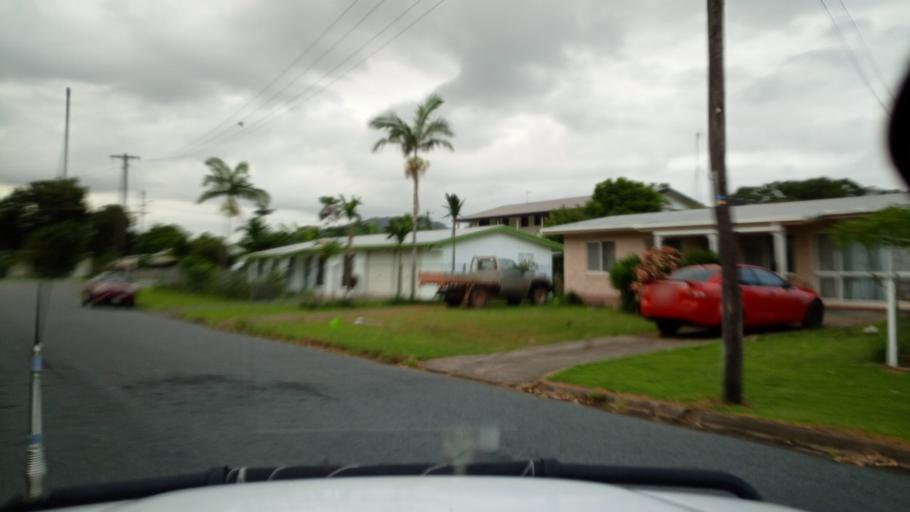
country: AU
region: Queensland
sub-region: Cairns
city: Woree
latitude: -16.9308
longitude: 145.7397
